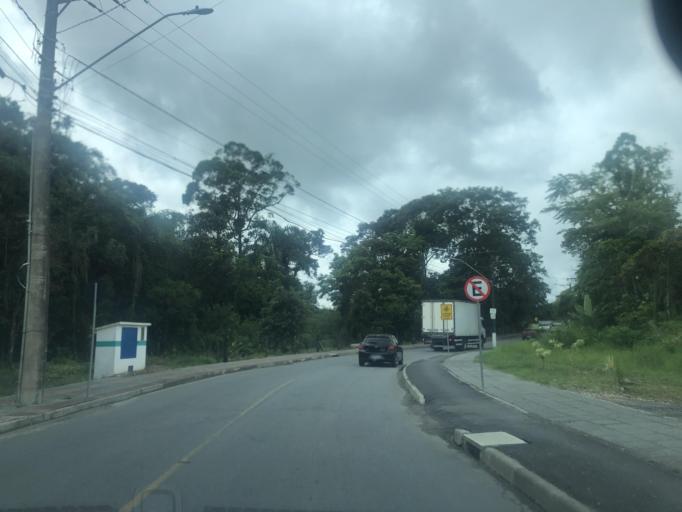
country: BR
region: Santa Catarina
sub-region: Joinville
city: Joinville
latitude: -26.3697
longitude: -48.7184
